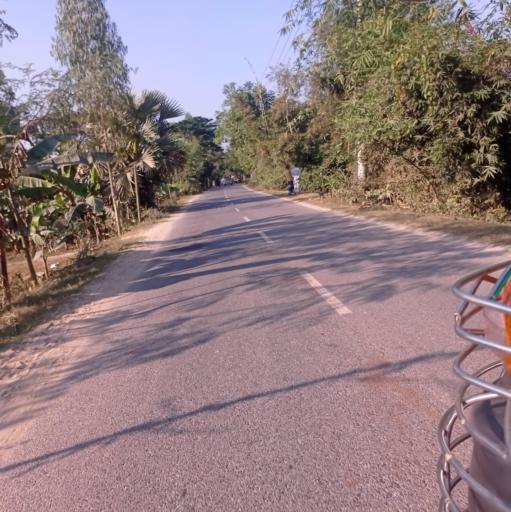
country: BD
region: Dhaka
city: Bajitpur
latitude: 24.1547
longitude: 90.8112
